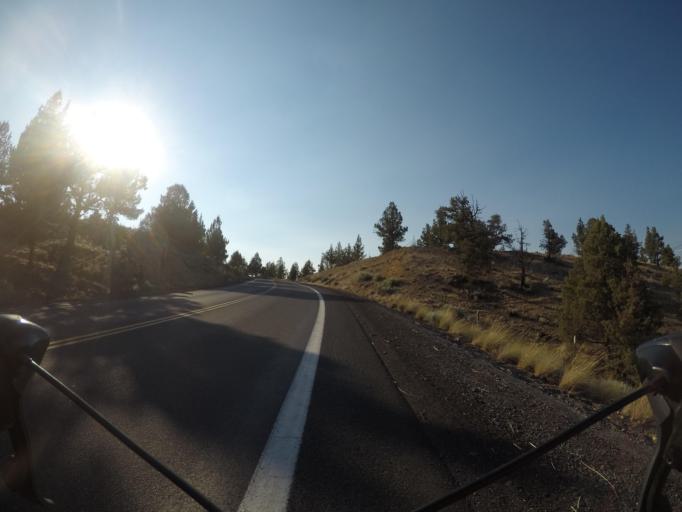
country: US
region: Oregon
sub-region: Deschutes County
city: Redmond
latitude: 44.2732
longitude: -121.2614
